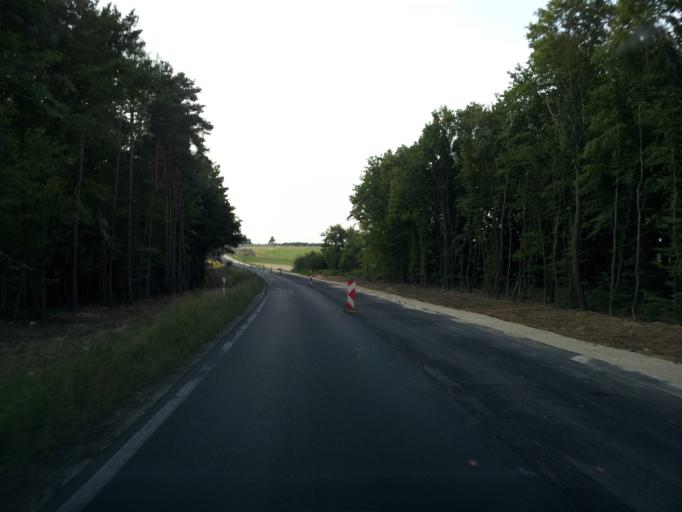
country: HU
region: Zala
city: Zalalovo
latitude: 46.8050
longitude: 16.5635
